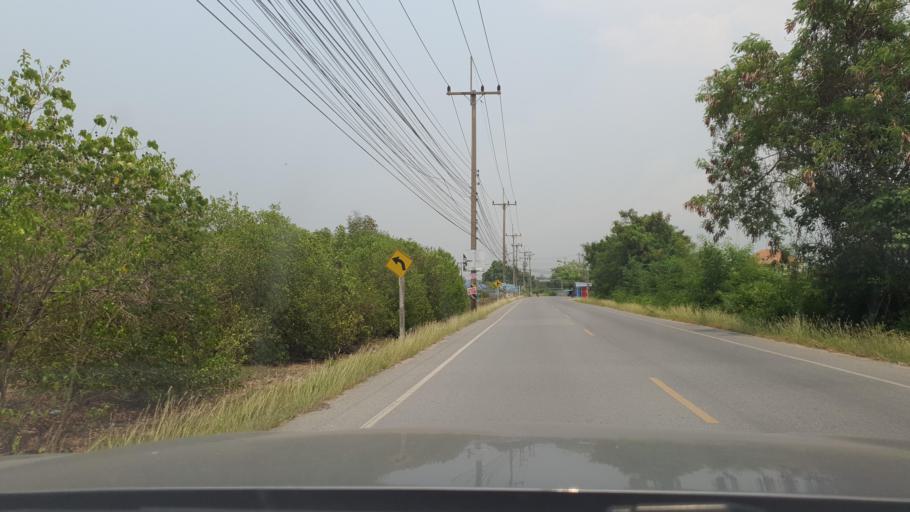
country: TH
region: Chachoengsao
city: Bang Pakong
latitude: 13.4838
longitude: 101.0127
